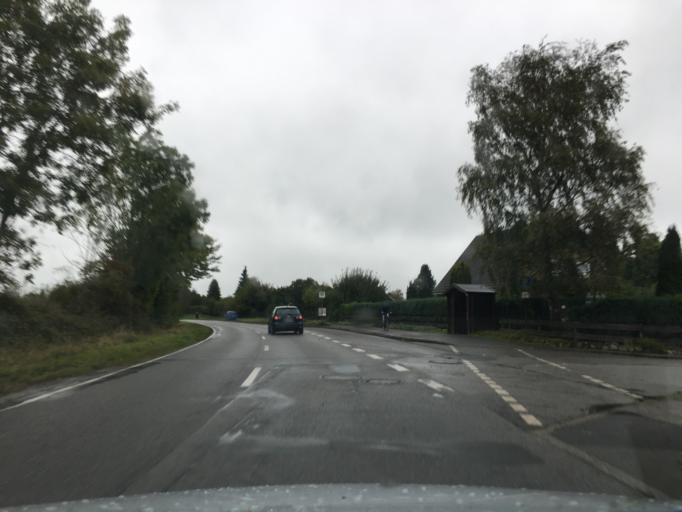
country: DE
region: Schleswig-Holstein
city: Ottendorf
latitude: 54.3660
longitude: 10.0452
